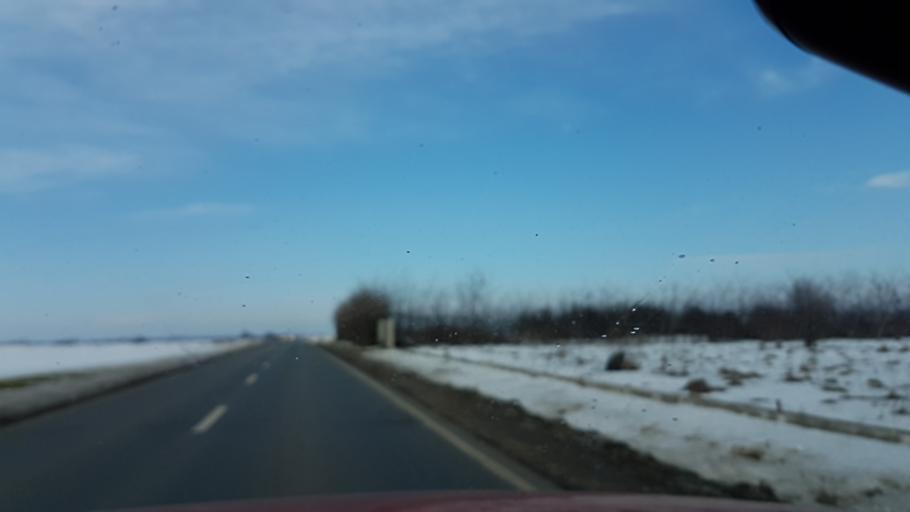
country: RO
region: Ilfov
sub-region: Comuna Tunari
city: Tunari
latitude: 44.5674
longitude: 26.1411
